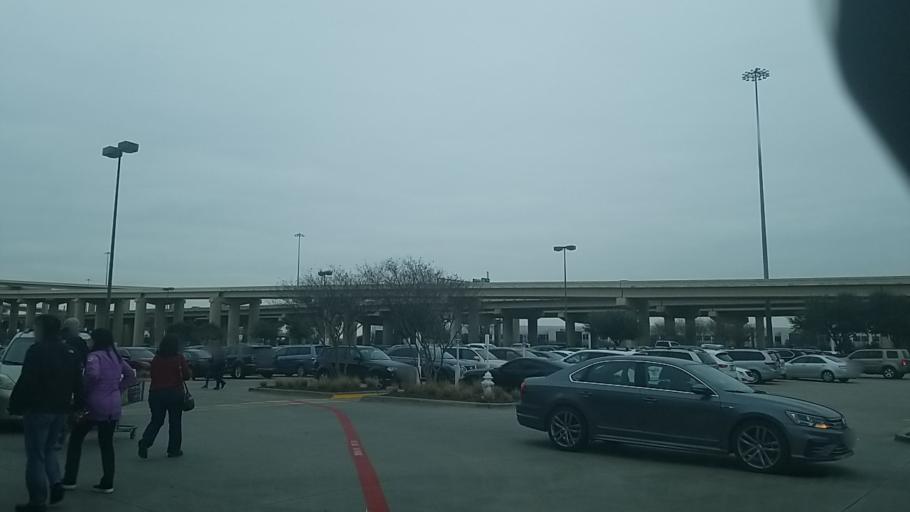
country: US
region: Texas
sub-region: Denton County
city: Lewisville
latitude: 32.9976
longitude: -96.9642
